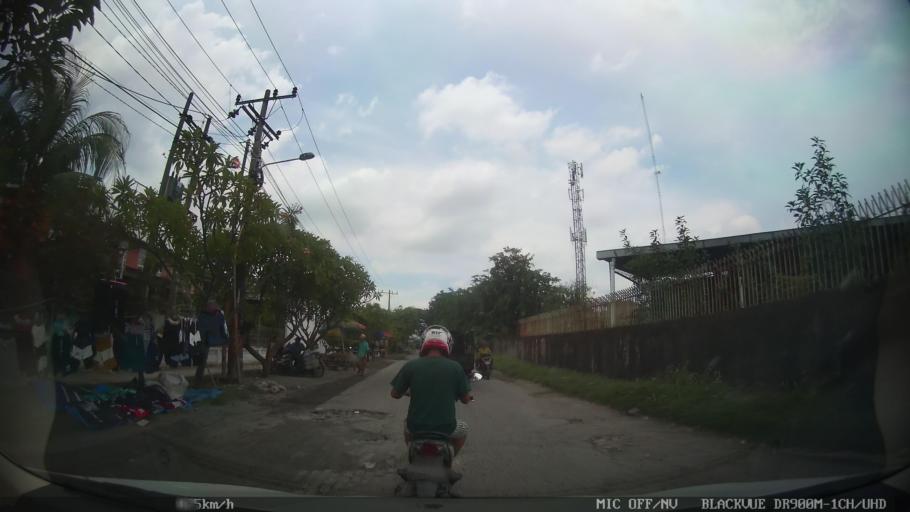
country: ID
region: North Sumatra
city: Labuhan Deli
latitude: 3.6739
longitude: 98.6755
